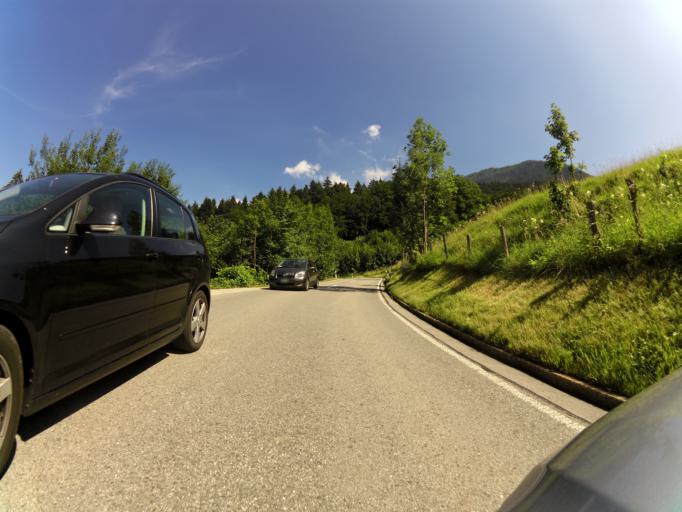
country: DE
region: Bavaria
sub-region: Upper Bavaria
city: Berchtesgaden
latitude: 47.6314
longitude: 13.0229
